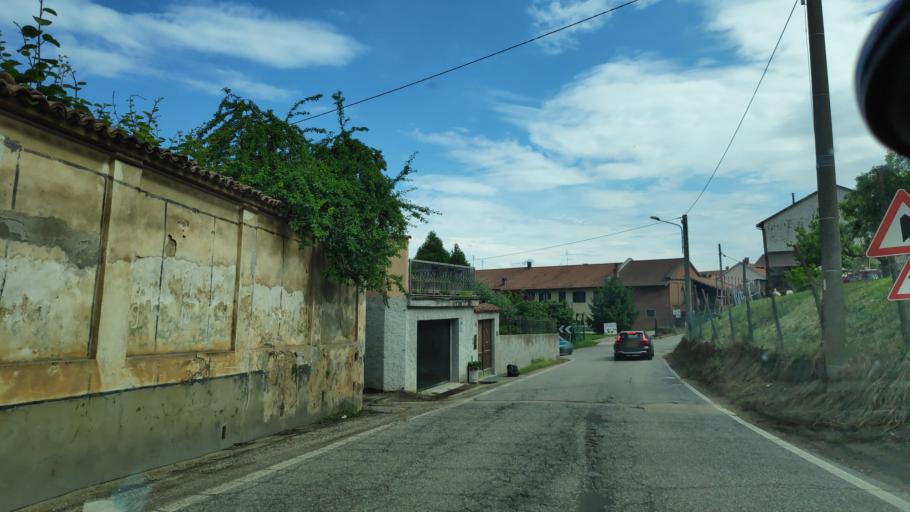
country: IT
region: Piedmont
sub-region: Provincia di Torino
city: Pecetto
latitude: 45.0060
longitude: 7.7626
